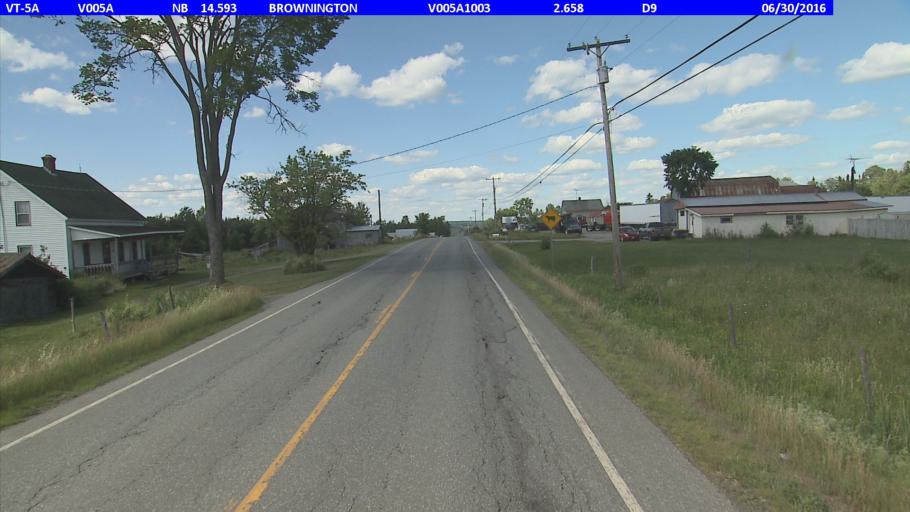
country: US
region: Vermont
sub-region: Orleans County
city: Newport
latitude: 44.8209
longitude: -72.0732
